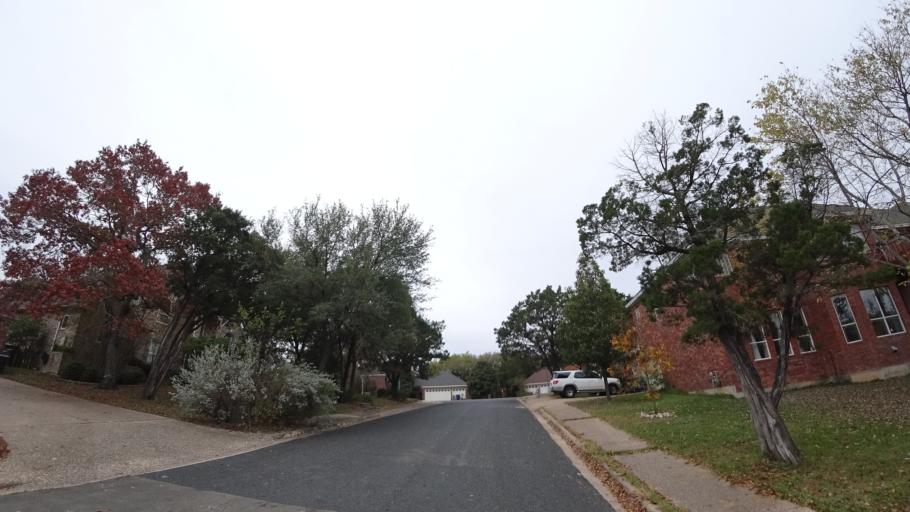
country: US
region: Texas
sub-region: Williamson County
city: Jollyville
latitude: 30.3891
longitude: -97.8001
